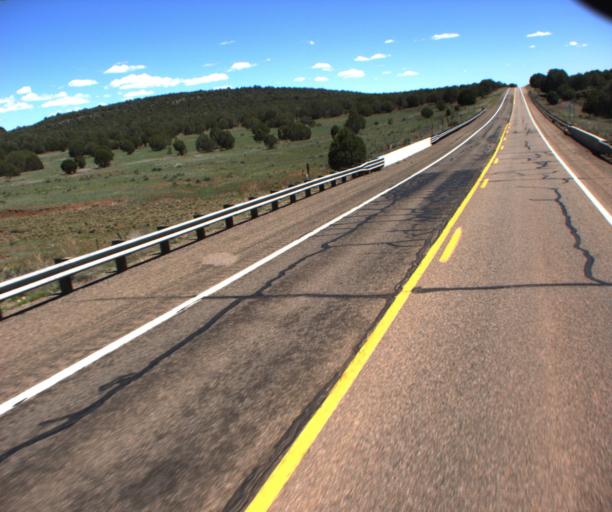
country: US
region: Arizona
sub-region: Yavapai County
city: Paulden
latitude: 35.1425
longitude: -112.4448
